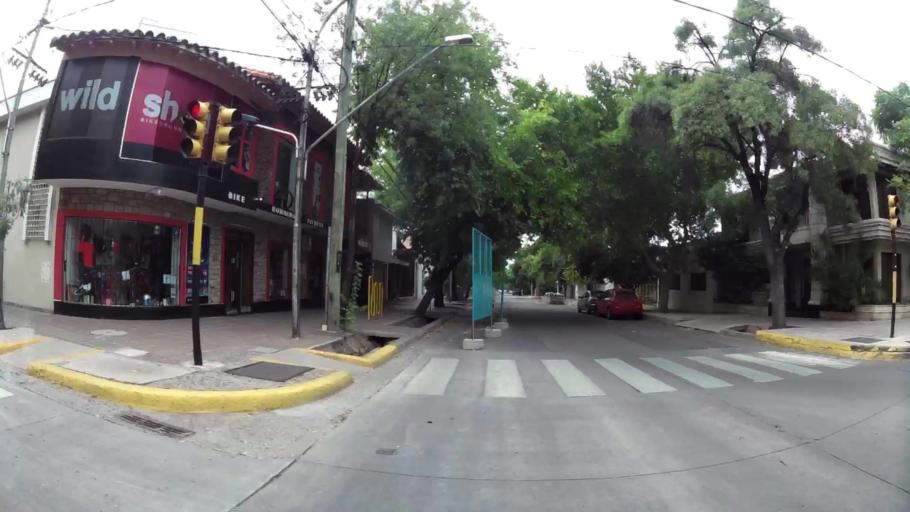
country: AR
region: Mendoza
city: Mendoza
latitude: -32.8848
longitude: -68.8588
